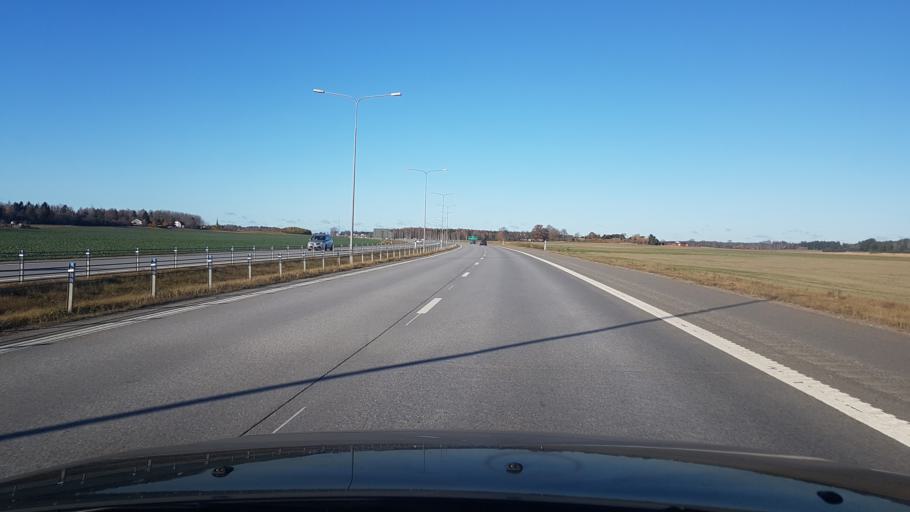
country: SE
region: Uppsala
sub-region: Uppsala Kommun
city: Saevja
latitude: 59.8567
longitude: 17.7304
